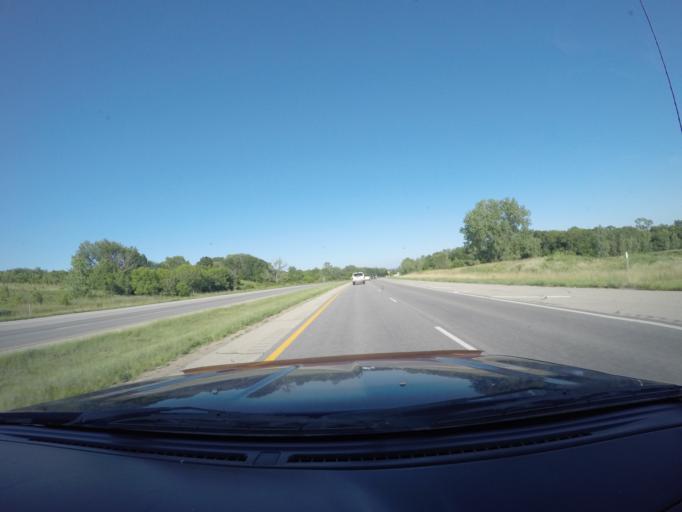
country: US
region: Kansas
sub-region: Shawnee County
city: Topeka
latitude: 39.0934
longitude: -95.6060
